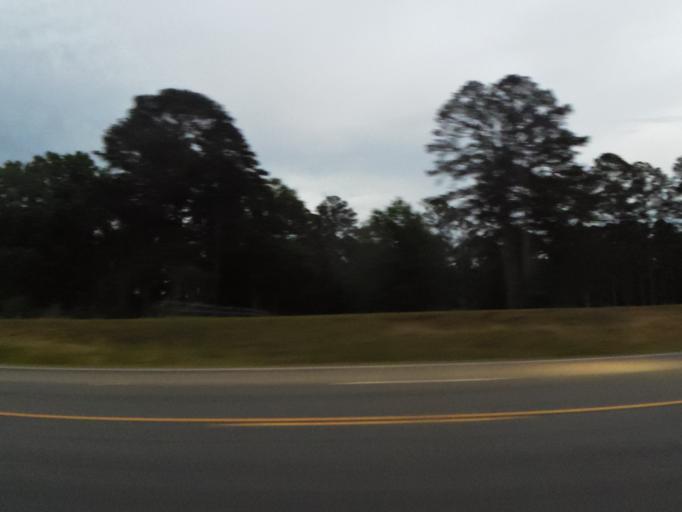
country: US
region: Georgia
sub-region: McDuffie County
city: Thomson
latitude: 33.5378
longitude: -82.5076
